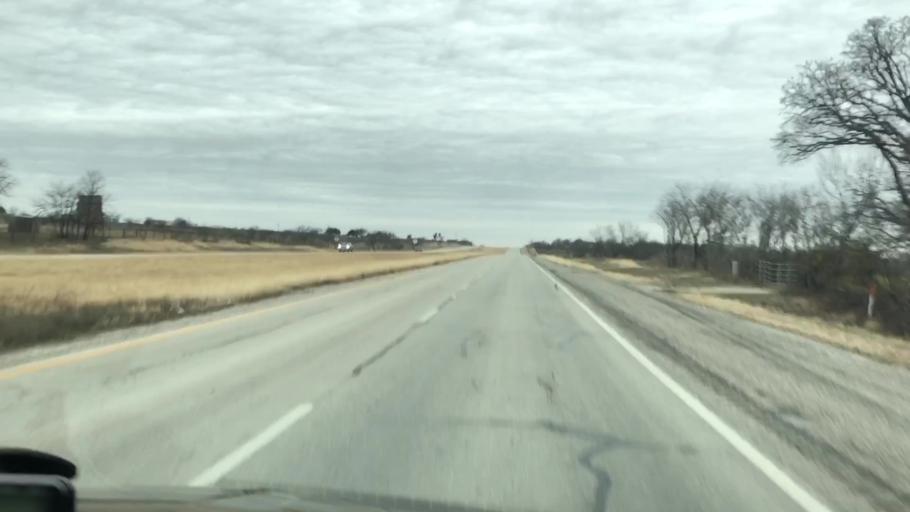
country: US
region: Texas
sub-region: Jack County
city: Jacksboro
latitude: 33.2410
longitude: -98.2191
